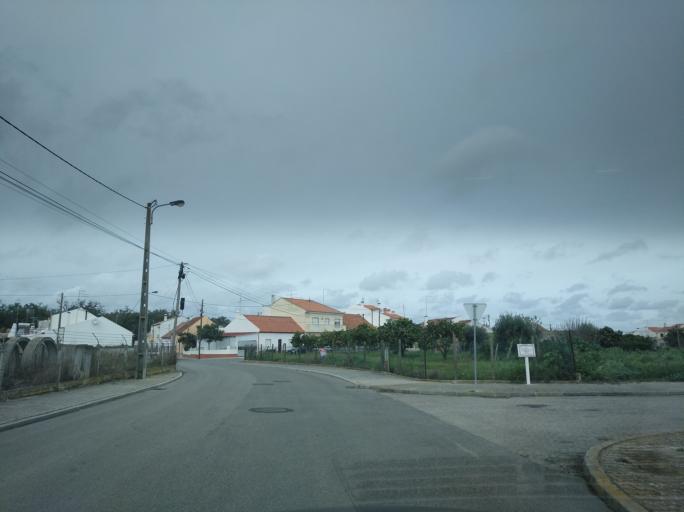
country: PT
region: Setubal
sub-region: Grandola
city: Grandola
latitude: 38.1815
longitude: -8.5717
